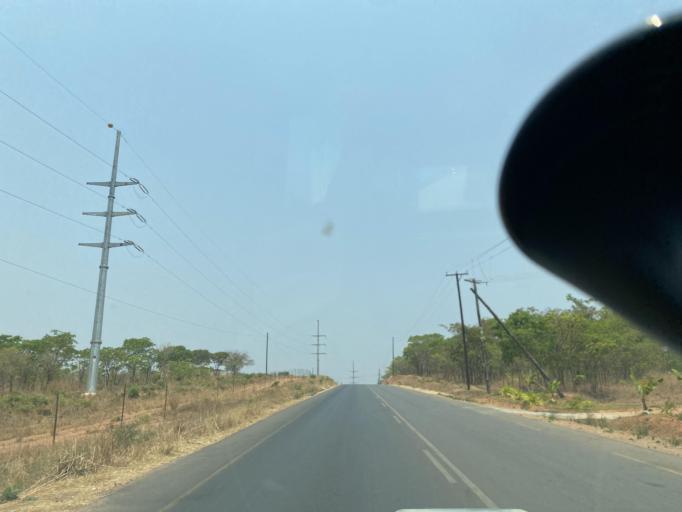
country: ZM
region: Lusaka
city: Lusaka
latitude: -15.5313
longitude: 28.4671
